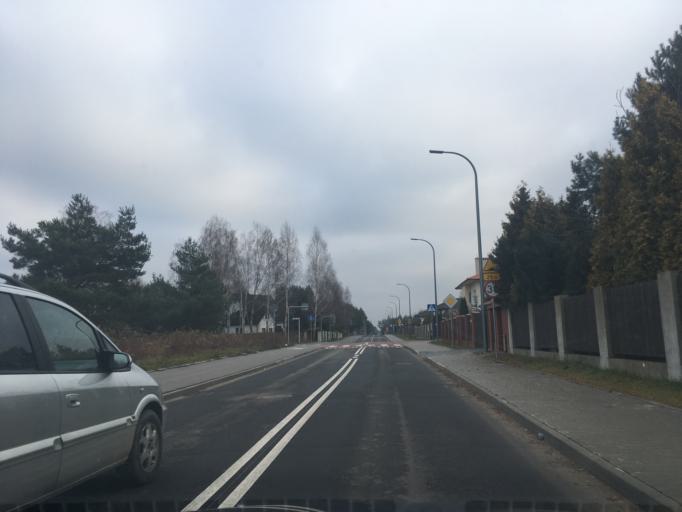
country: PL
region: Masovian Voivodeship
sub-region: Powiat piaseczynski
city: Lesznowola
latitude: 52.0713
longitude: 20.9690
